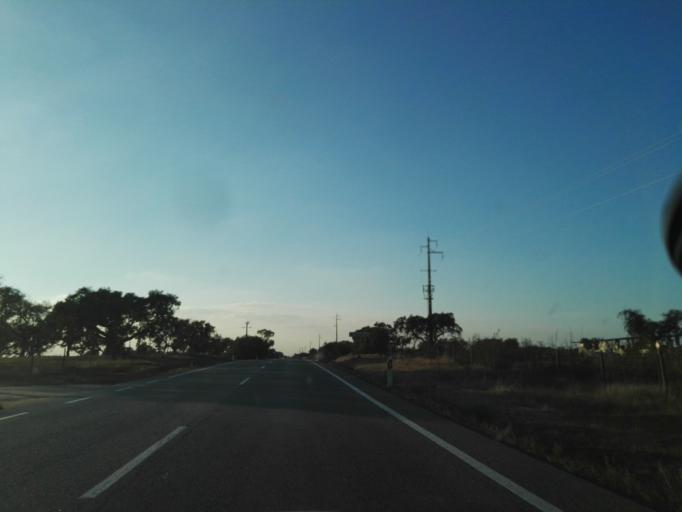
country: PT
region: Evora
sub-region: Arraiolos
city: Arraiolos
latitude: 38.8451
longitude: -7.8818
